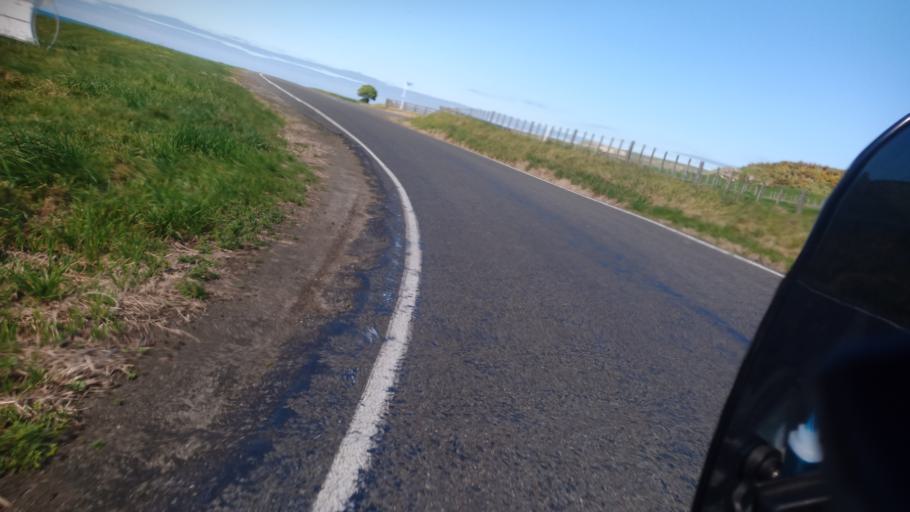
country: NZ
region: Gisborne
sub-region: Gisborne District
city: Gisborne
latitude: -39.0894
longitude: 177.9591
